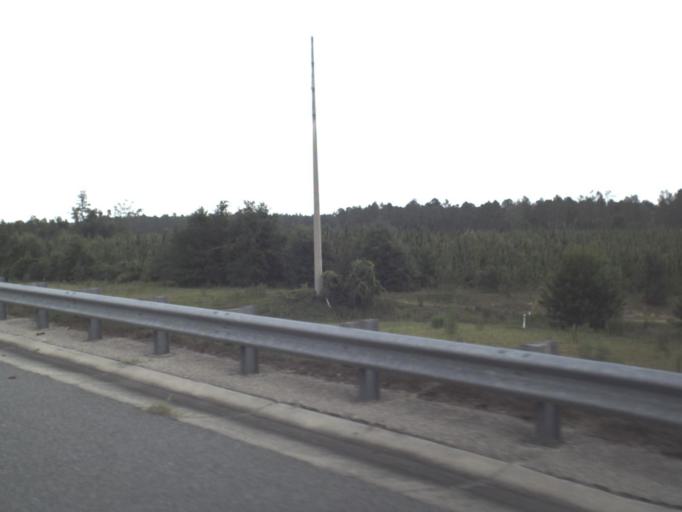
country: US
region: Florida
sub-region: Madison County
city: Madison
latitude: 30.3962
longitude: -83.2052
